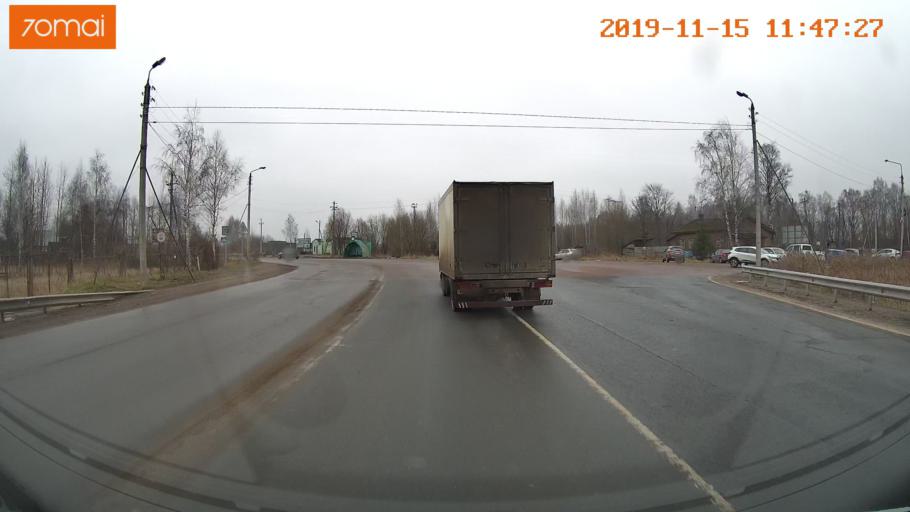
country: RU
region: Vologda
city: Vologda
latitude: 59.2387
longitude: 39.7949
